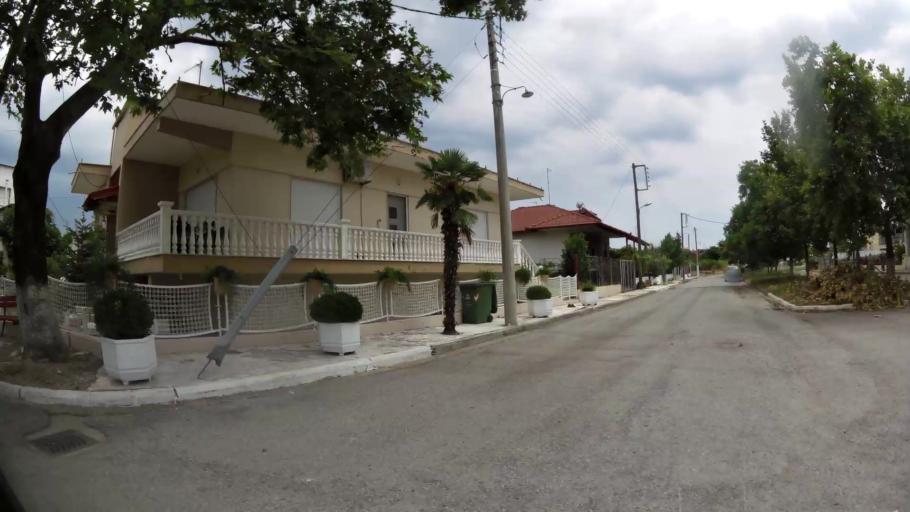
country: GR
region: Central Macedonia
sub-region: Nomos Pierias
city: Kallithea
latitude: 40.2757
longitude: 22.5794
